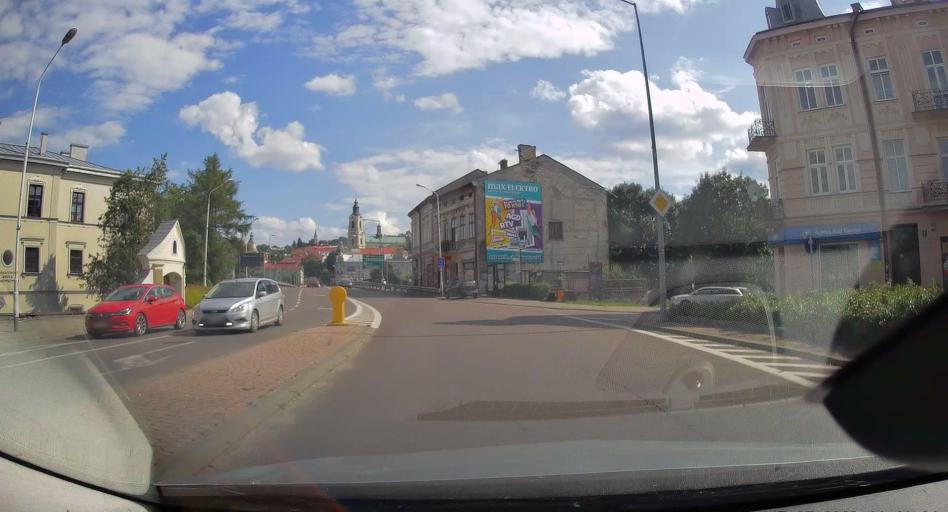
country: PL
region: Subcarpathian Voivodeship
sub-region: Przemysl
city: Przemysl
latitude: 49.7860
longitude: 22.7665
